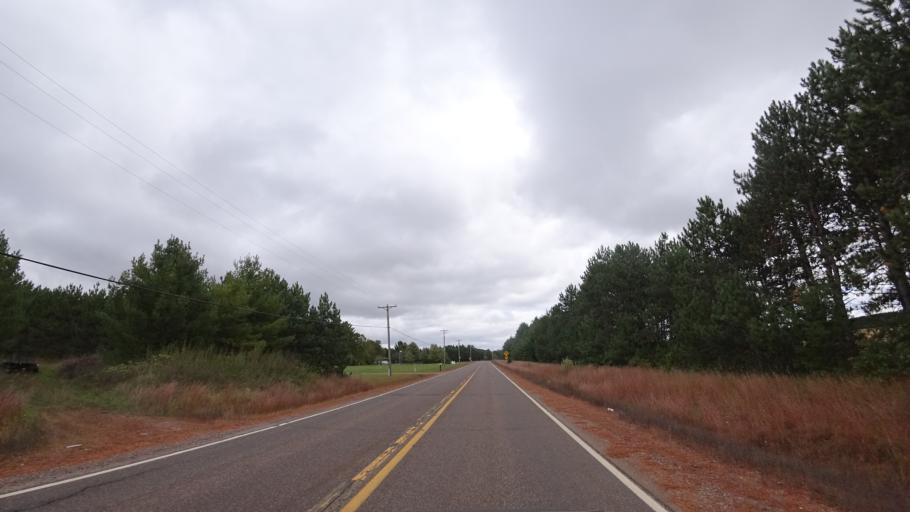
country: US
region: Wisconsin
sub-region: Chippewa County
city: Lake Wissota
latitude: 44.9446
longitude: -91.2664
